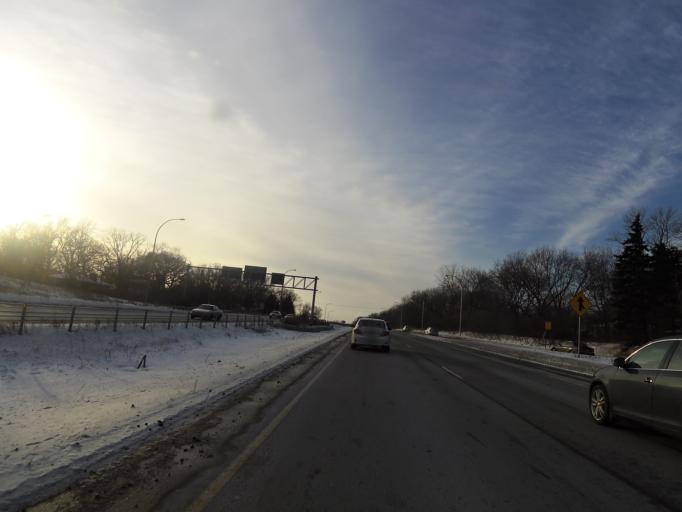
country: US
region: Minnesota
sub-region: Hennepin County
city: Edina
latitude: 44.8900
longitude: -93.3527
